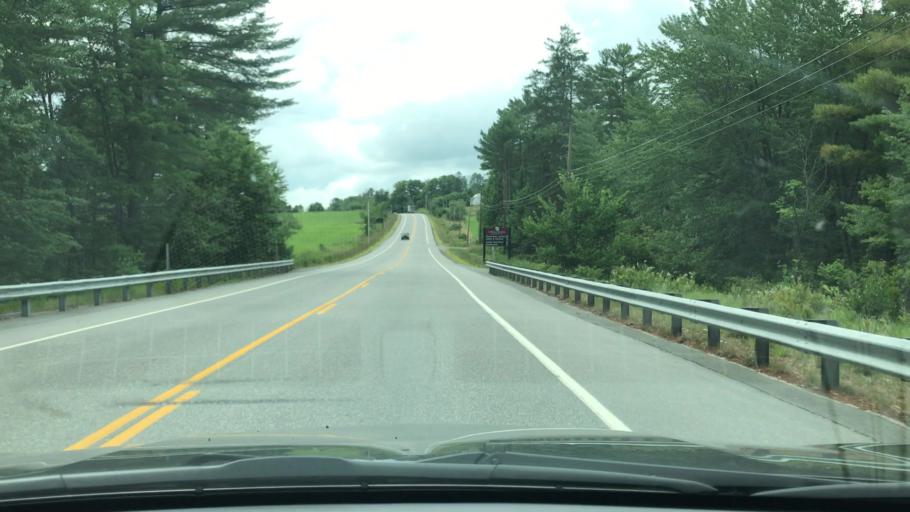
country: US
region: Maine
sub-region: Oxford County
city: Bethel
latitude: 44.4198
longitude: -70.7494
